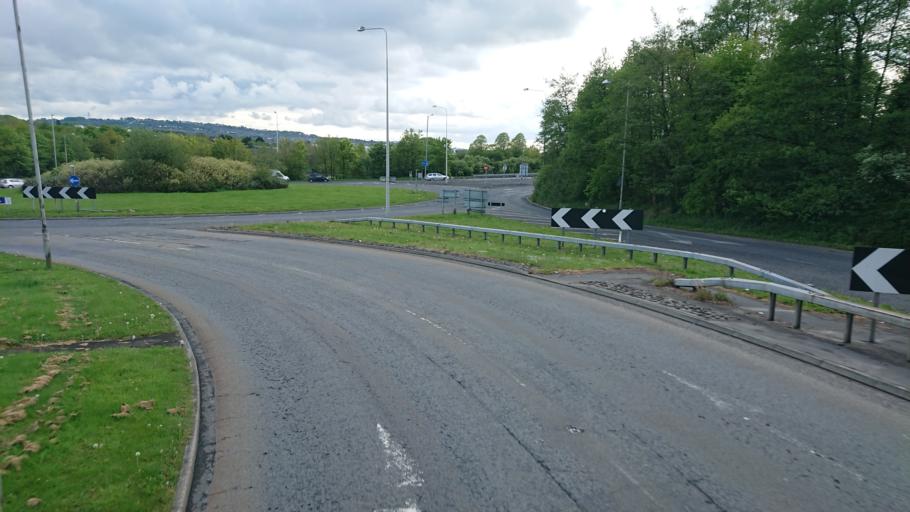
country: GB
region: England
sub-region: Lancashire
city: Colne
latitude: 53.8549
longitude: -2.1908
